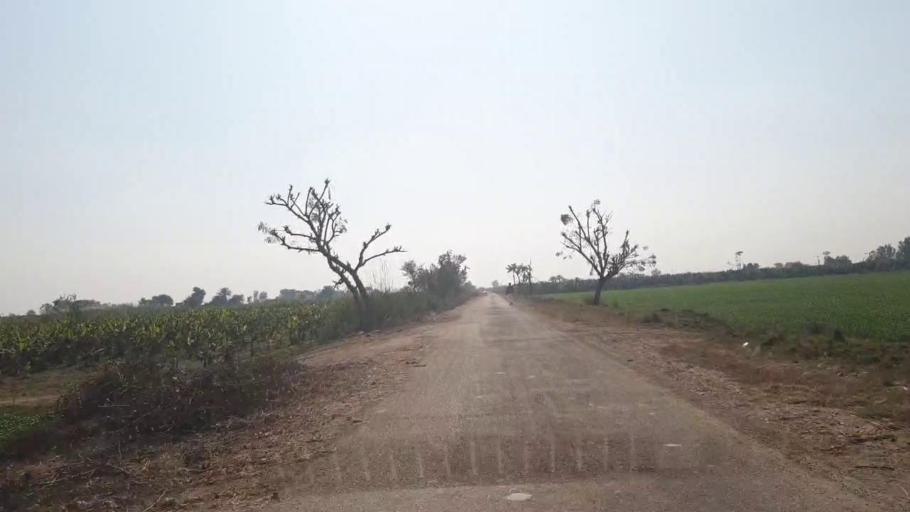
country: PK
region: Sindh
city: Sakrand
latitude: 26.0328
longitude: 68.4379
